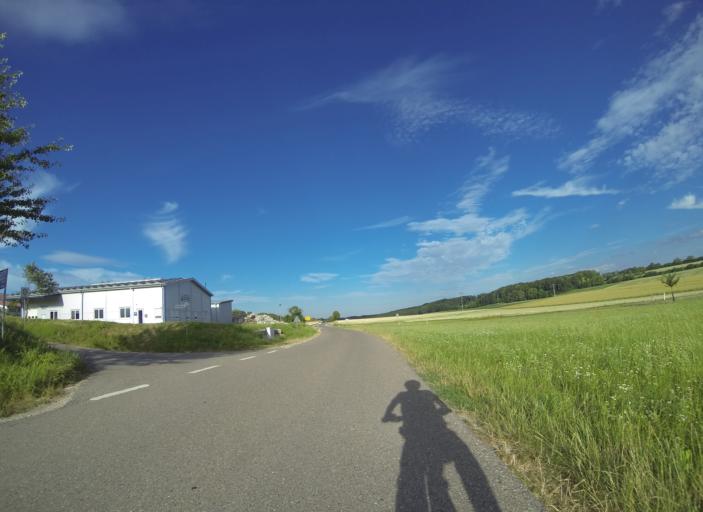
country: DE
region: Baden-Wuerttemberg
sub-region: Tuebingen Region
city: Altheim
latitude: 48.3268
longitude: 9.7748
